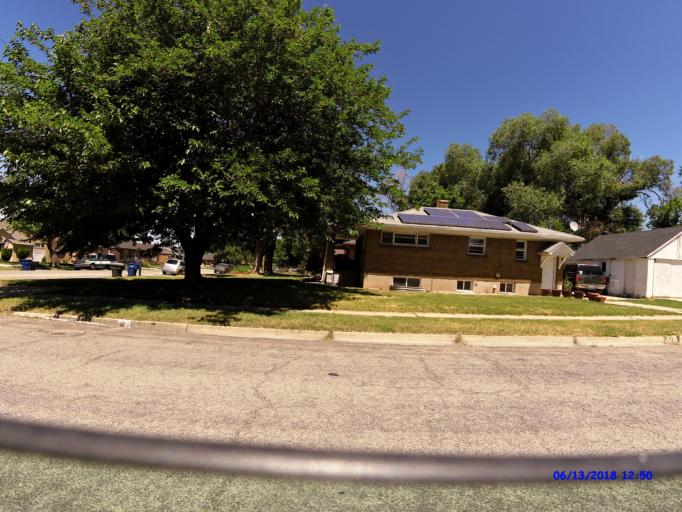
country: US
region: Utah
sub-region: Weber County
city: Ogden
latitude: 41.2090
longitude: -111.9539
